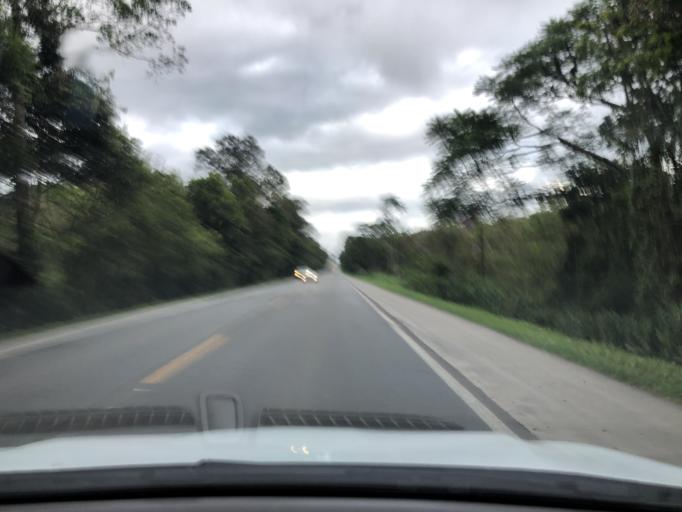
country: BR
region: Santa Catarina
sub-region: Sao Francisco Do Sul
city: Sao Francisco do Sul
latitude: -26.3190
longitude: -48.6468
